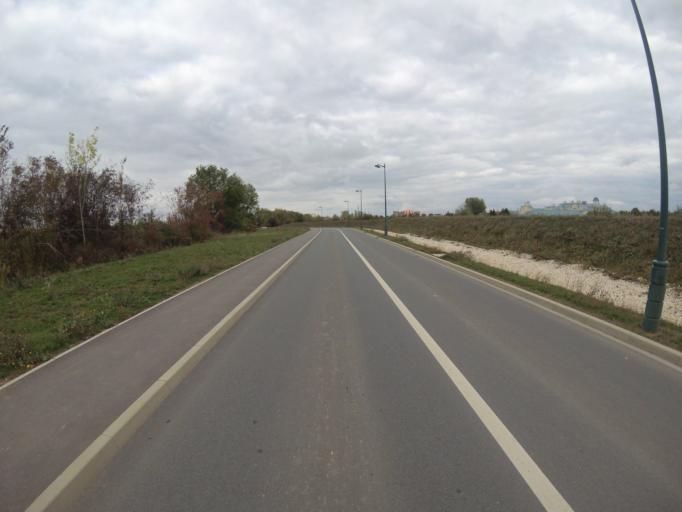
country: FR
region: Ile-de-France
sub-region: Departement de Seine-et-Marne
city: Serris
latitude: 48.8626
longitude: 2.7838
